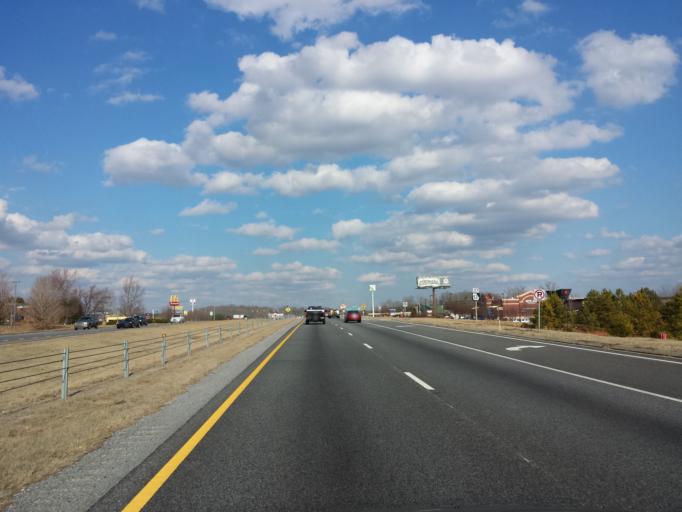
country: US
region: Georgia
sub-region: Dawson County
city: Dawsonville
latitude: 34.3608
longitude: -84.0401
